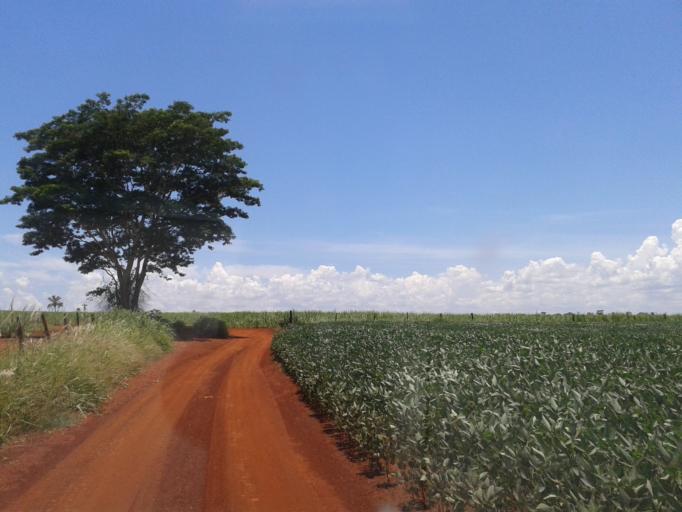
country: BR
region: Minas Gerais
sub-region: Centralina
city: Centralina
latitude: -18.6165
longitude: -49.2842
